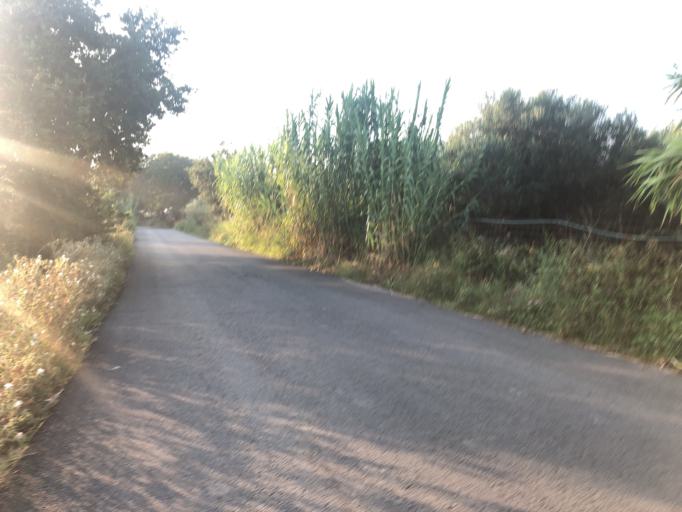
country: GR
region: Crete
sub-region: Nomos Chanias
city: Georgioupolis
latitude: 35.3502
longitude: 24.2794
